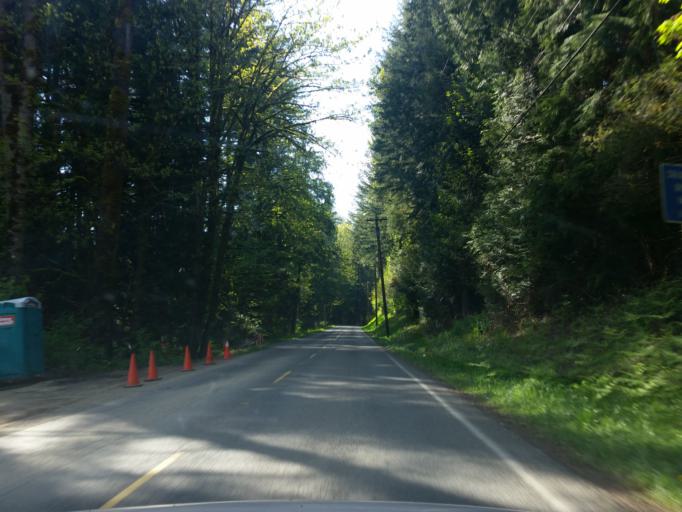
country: US
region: Washington
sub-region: Snohomish County
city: Three Lakes
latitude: 47.9612
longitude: -121.9620
